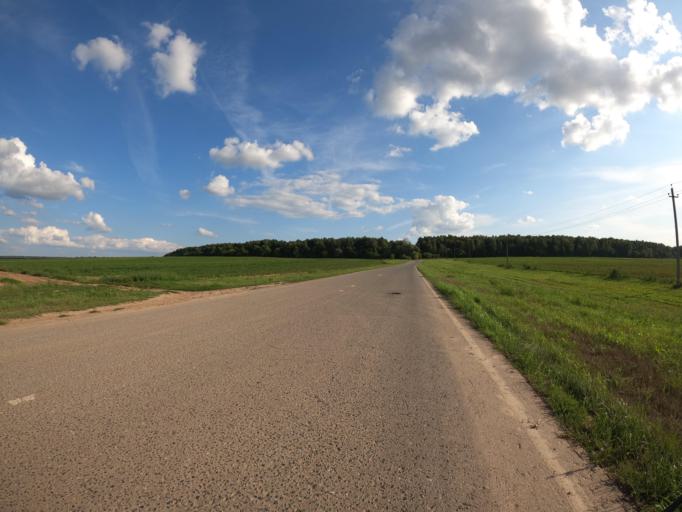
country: RU
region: Moskovskaya
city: Meshcherino
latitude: 55.1846
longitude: 38.4715
